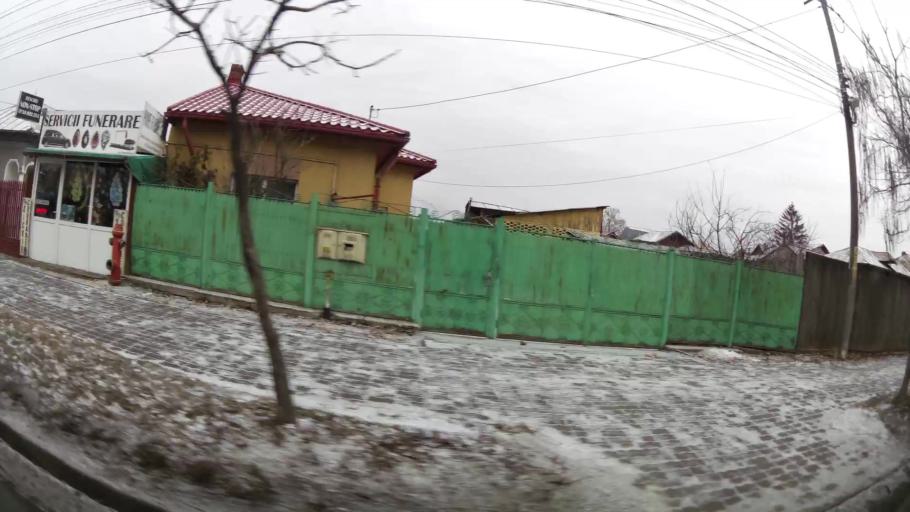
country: RO
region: Dambovita
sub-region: Comuna Ulmi
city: Ulmi
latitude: 44.9109
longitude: 25.4867
